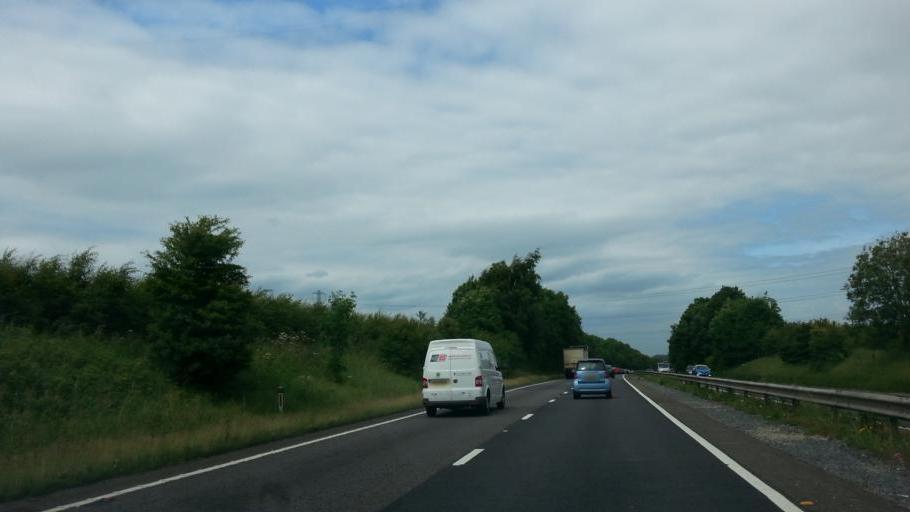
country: GB
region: England
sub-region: Derbyshire
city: Melbourne
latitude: 52.7875
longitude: -1.4098
